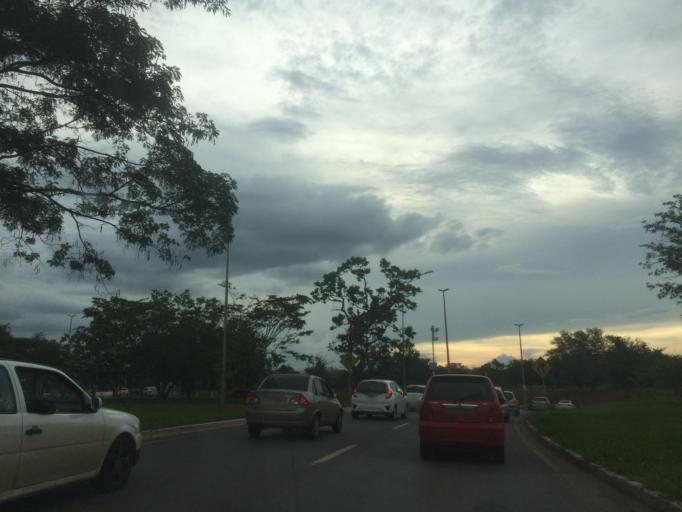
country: BR
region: Federal District
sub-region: Brasilia
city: Brasilia
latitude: -15.8042
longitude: -47.8533
